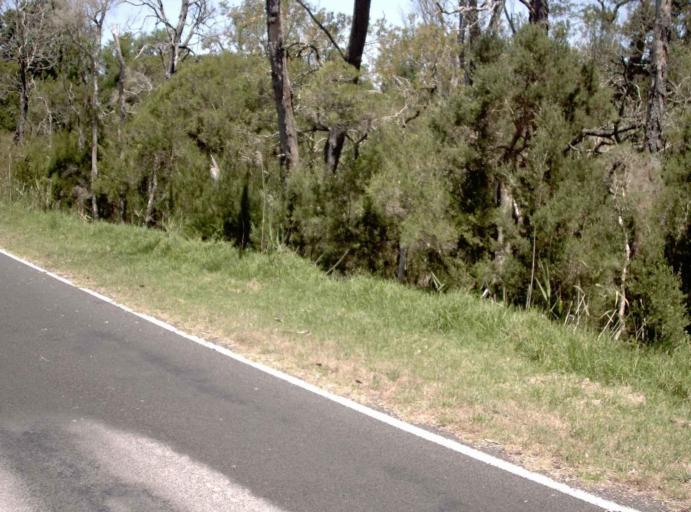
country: AU
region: Victoria
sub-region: Latrobe
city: Morwell
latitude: -38.8570
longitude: 146.2474
